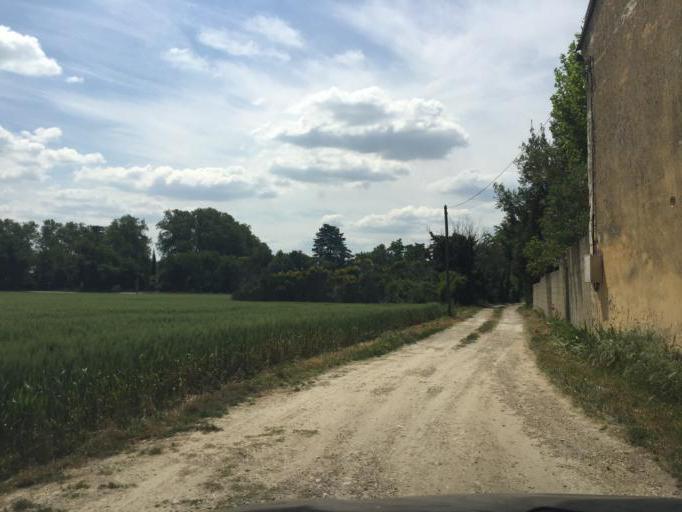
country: FR
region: Provence-Alpes-Cote d'Azur
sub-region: Departement du Vaucluse
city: Jonquieres
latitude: 44.1347
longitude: 4.9114
